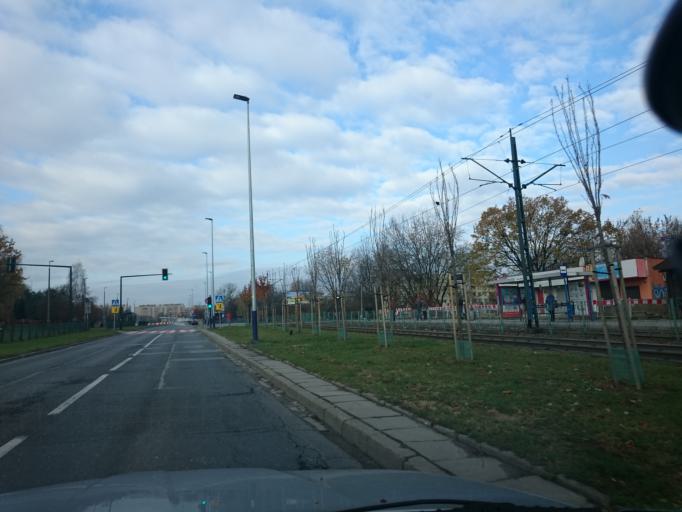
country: PL
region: Lesser Poland Voivodeship
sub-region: Powiat wielicki
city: Czarnochowice
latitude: 50.0157
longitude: 20.0204
